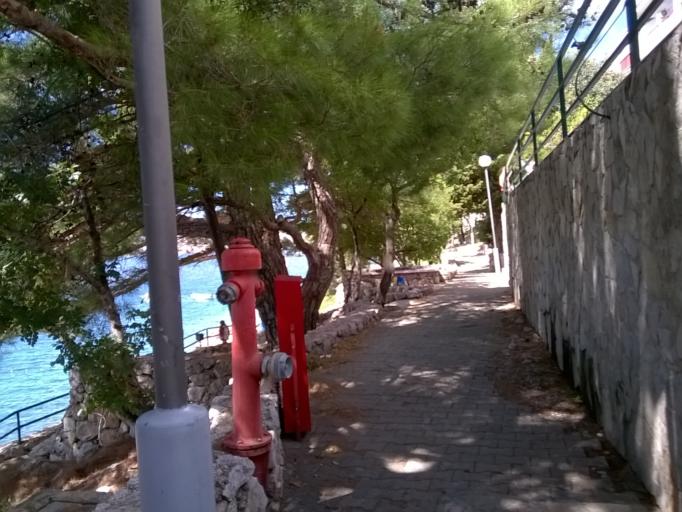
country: HR
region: Licko-Senjska
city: Karlobag
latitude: 44.5292
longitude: 15.0683
